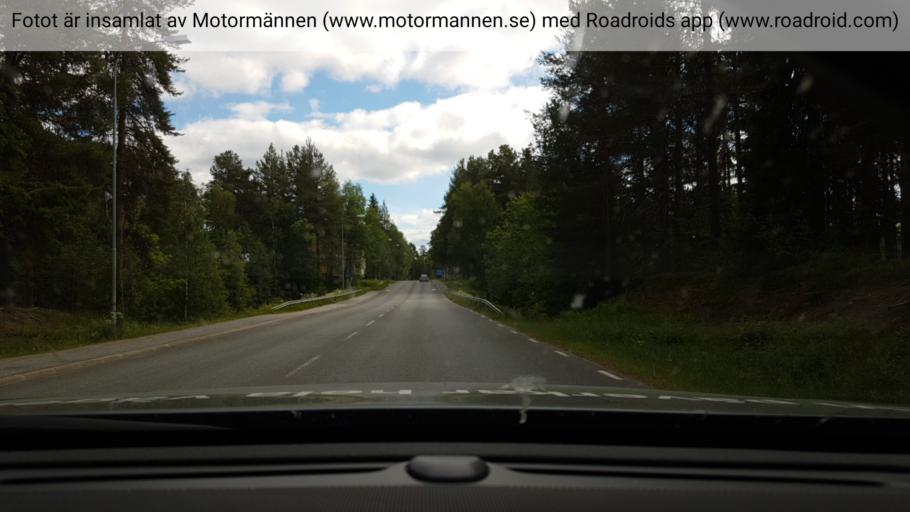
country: SE
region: Vaesterbotten
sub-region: Sorsele Kommun
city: Sorsele
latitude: 65.5402
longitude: 17.5410
